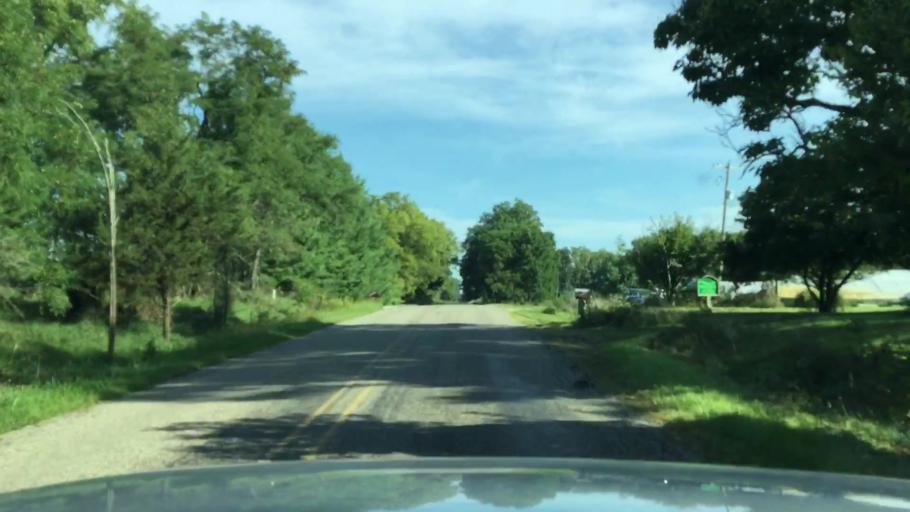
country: US
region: Michigan
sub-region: Lenawee County
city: Hudson
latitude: 41.8736
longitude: -84.4201
